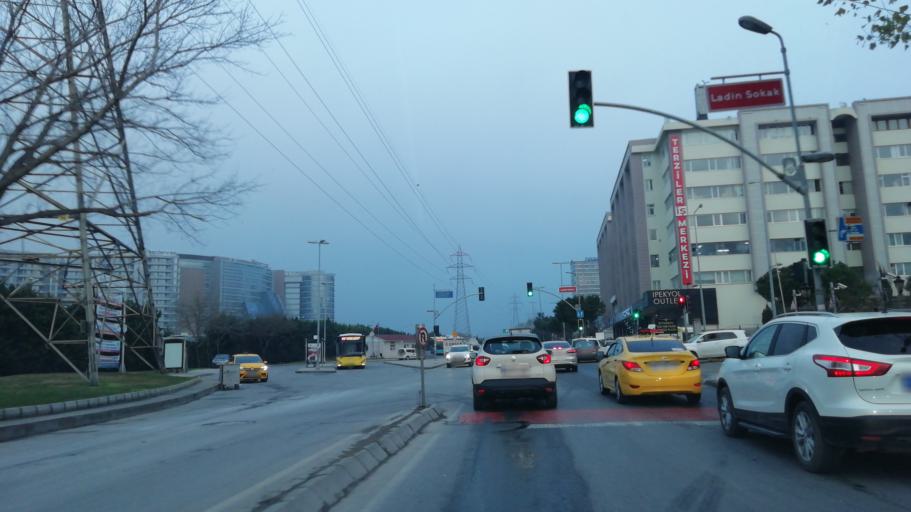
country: TR
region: Istanbul
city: Bahcelievler
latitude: 41.0032
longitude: 28.8154
